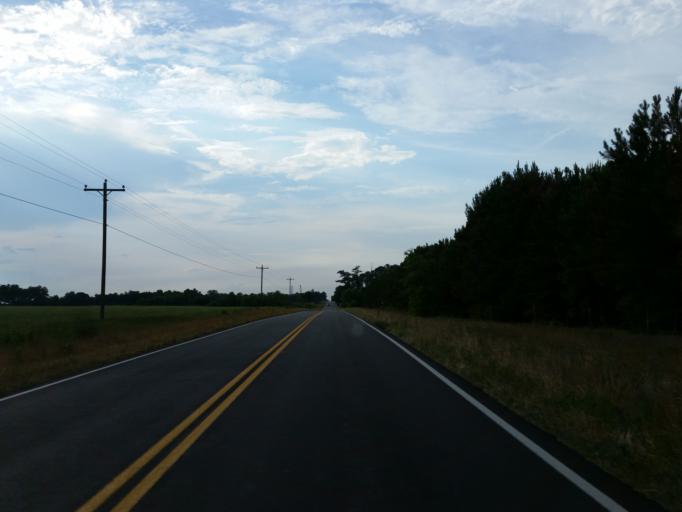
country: US
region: Georgia
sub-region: Dooly County
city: Unadilla
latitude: 32.2876
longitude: -83.7498
